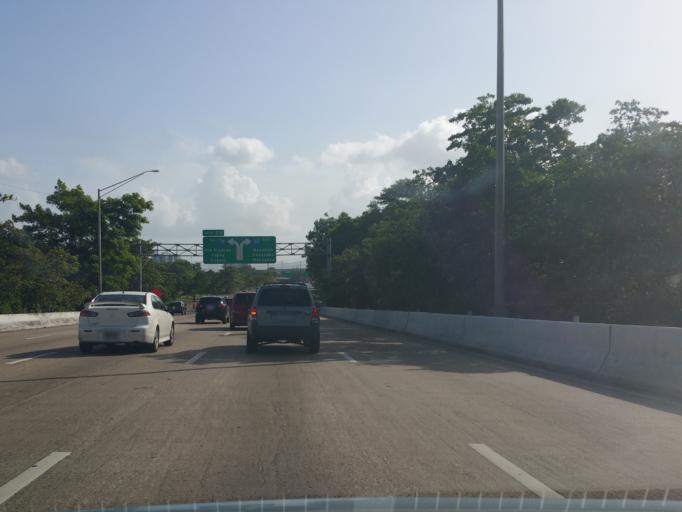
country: PR
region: San Juan
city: San Juan
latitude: 18.4366
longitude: -66.0729
